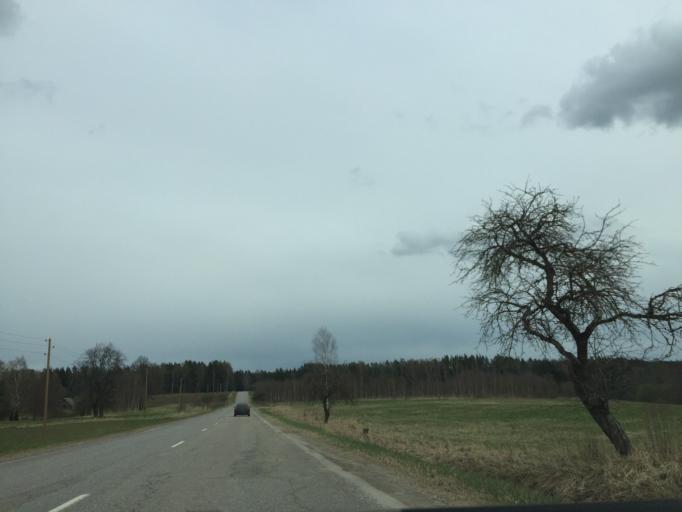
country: LV
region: Priekuli
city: Priekuli
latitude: 57.3226
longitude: 25.3781
